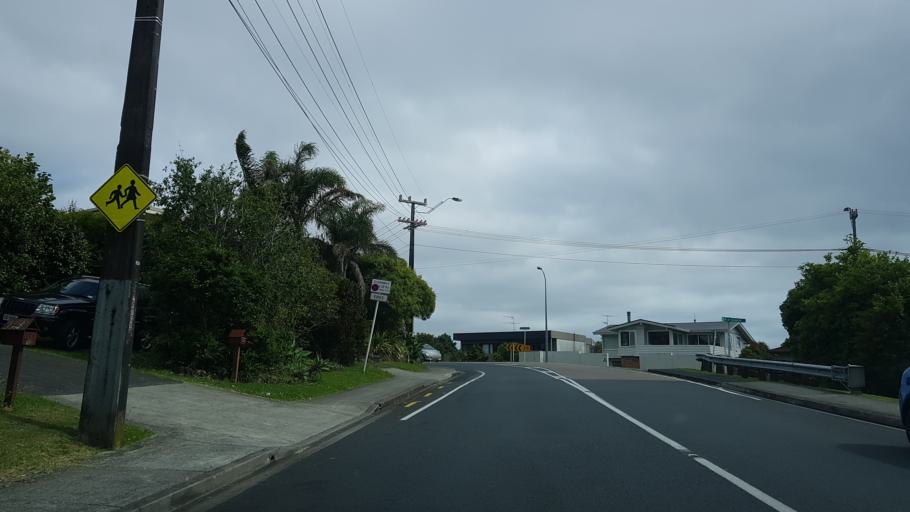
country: NZ
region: Auckland
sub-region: Auckland
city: North Shore
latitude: -36.8068
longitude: 174.7533
